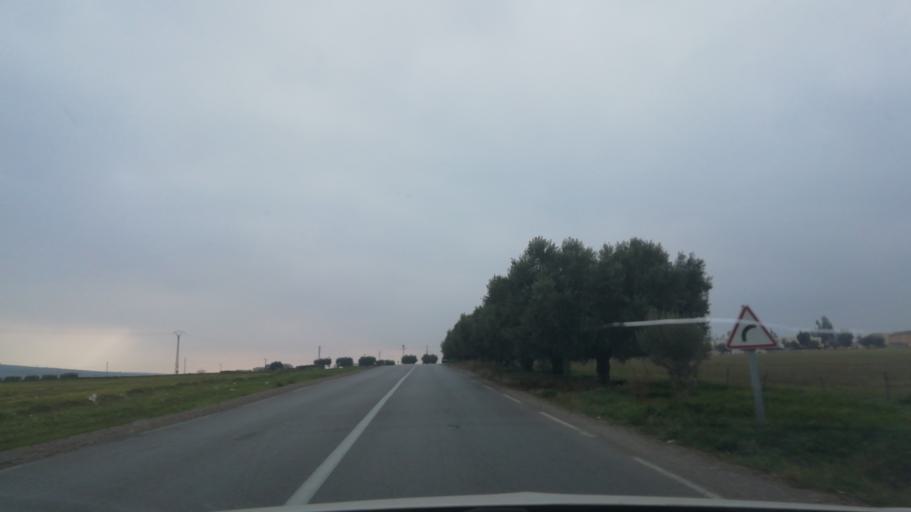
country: DZ
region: Sidi Bel Abbes
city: Sfizef
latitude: 35.2554
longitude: -0.1880
